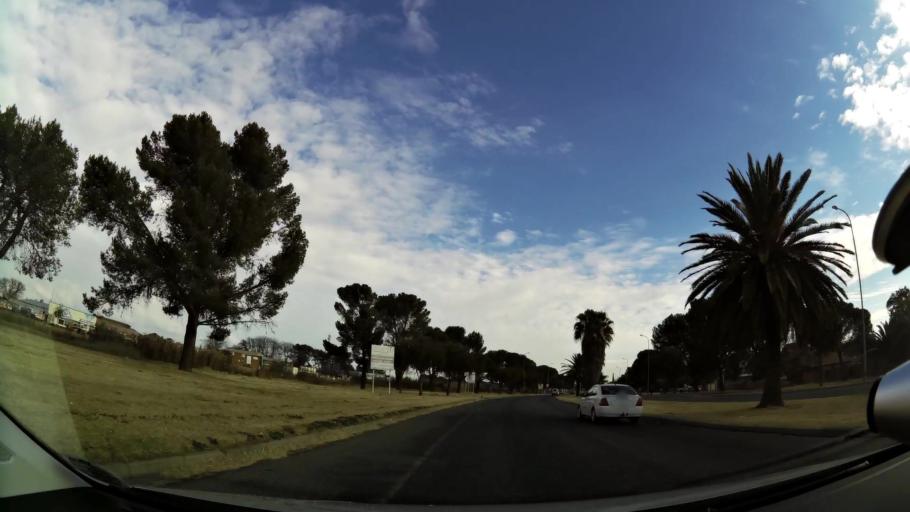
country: ZA
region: Orange Free State
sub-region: Lejweleputswa District Municipality
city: Welkom
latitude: -27.9840
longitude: 26.7598
